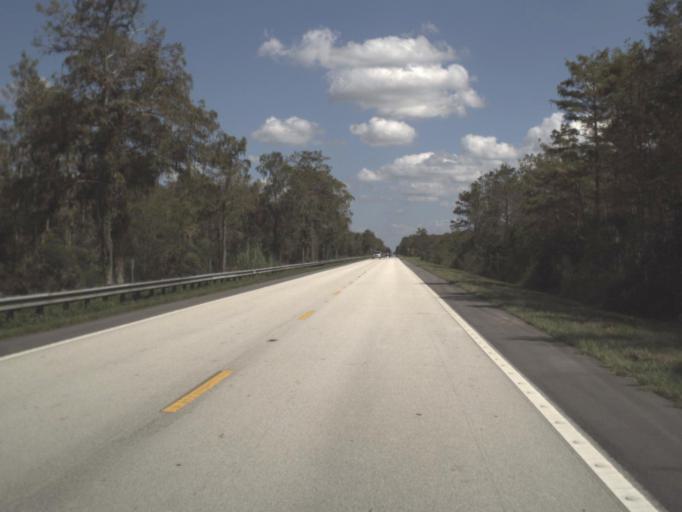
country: US
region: Florida
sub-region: Miami-Dade County
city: Kendall West
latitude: 25.8527
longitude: -80.9927
